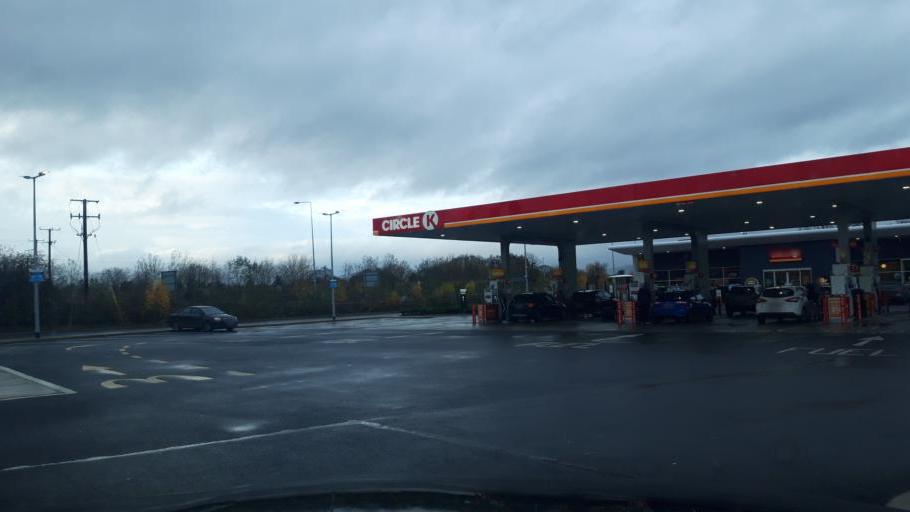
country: IE
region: Leinster
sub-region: County Carlow
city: Carlow
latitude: 52.8025
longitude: -6.8822
